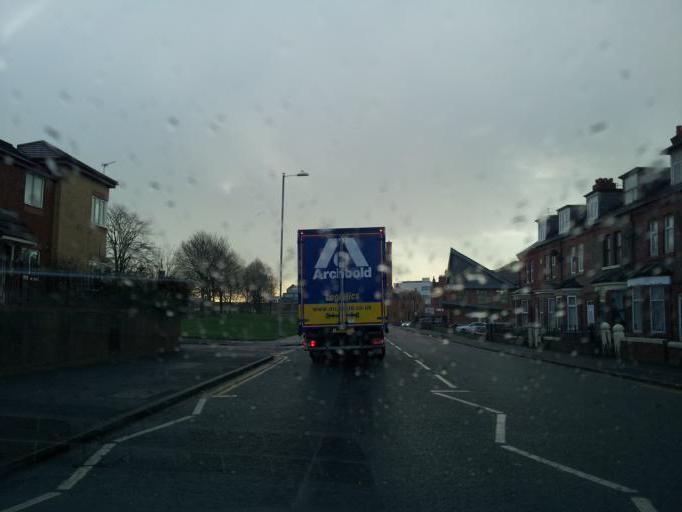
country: GB
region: England
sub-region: Manchester
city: Blackley
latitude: 53.5167
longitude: -2.2131
